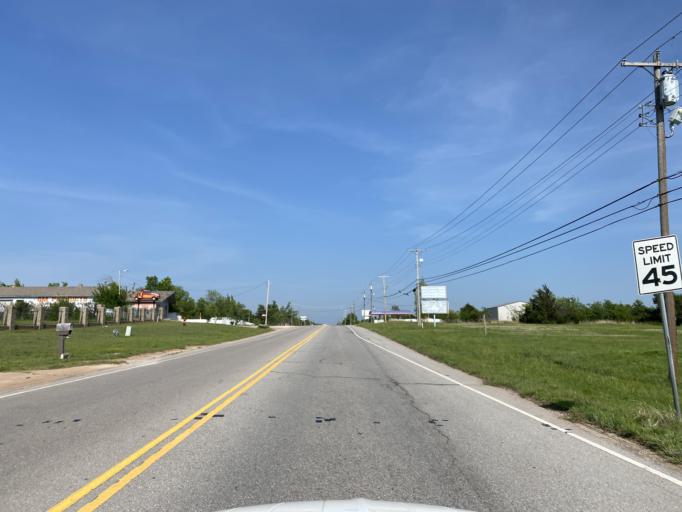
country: US
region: Oklahoma
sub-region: Oklahoma County
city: Midwest City
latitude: 35.4352
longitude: -97.3516
